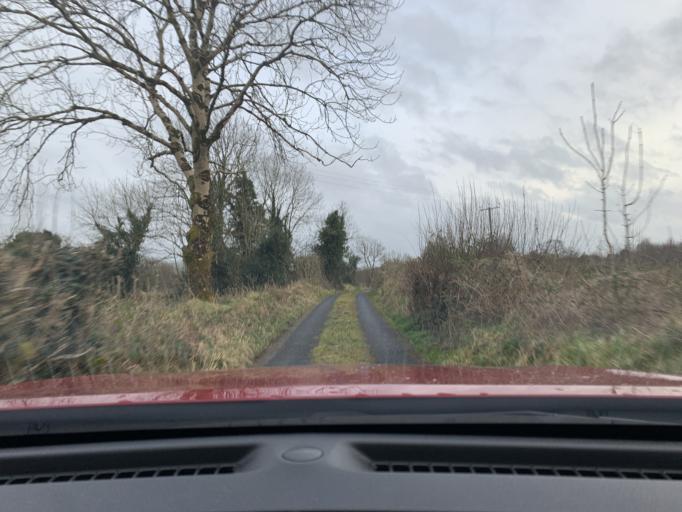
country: IE
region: Connaught
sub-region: Sligo
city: Ballymote
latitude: 53.9696
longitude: -8.4702
